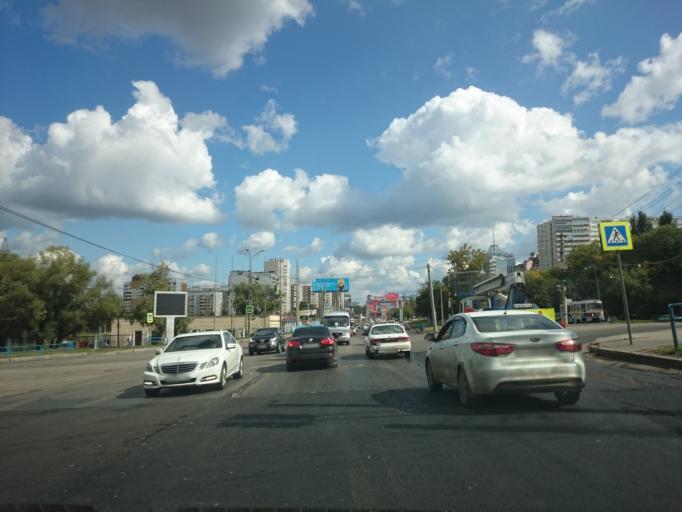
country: RU
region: Samara
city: Samara
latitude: 53.2340
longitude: 50.1858
